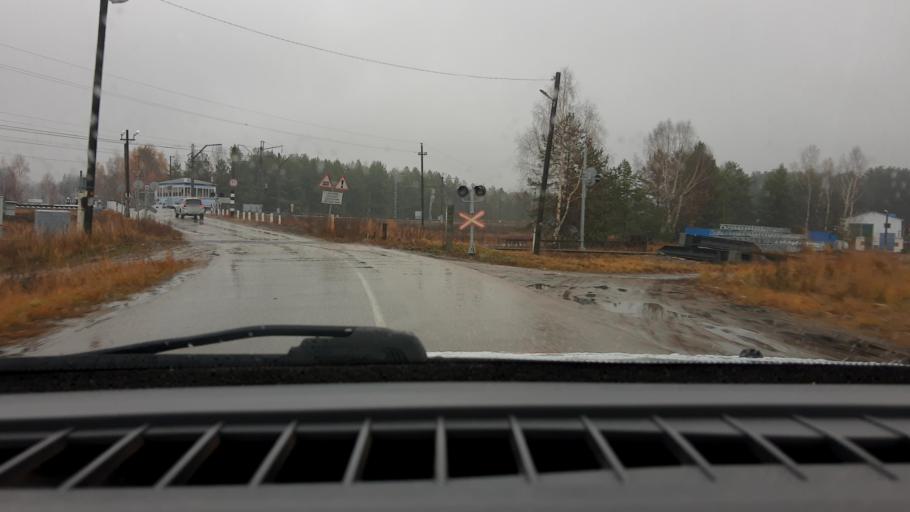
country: RU
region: Nizjnij Novgorod
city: Linda
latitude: 56.6843
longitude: 44.2019
